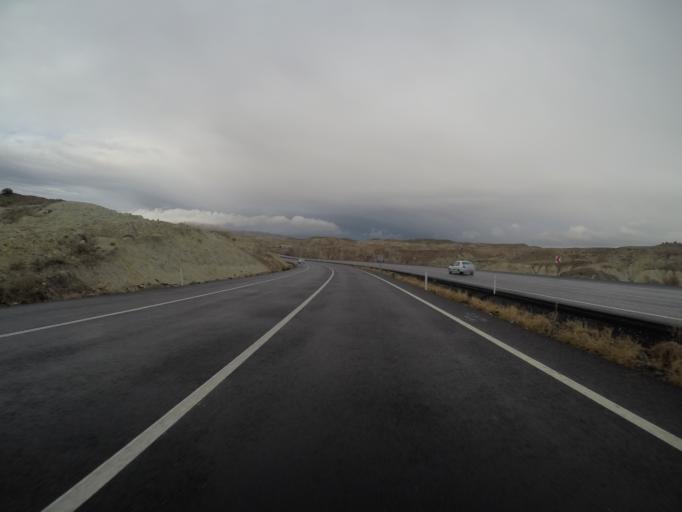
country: TR
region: Nevsehir
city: Avanos
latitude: 38.6910
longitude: 34.8157
